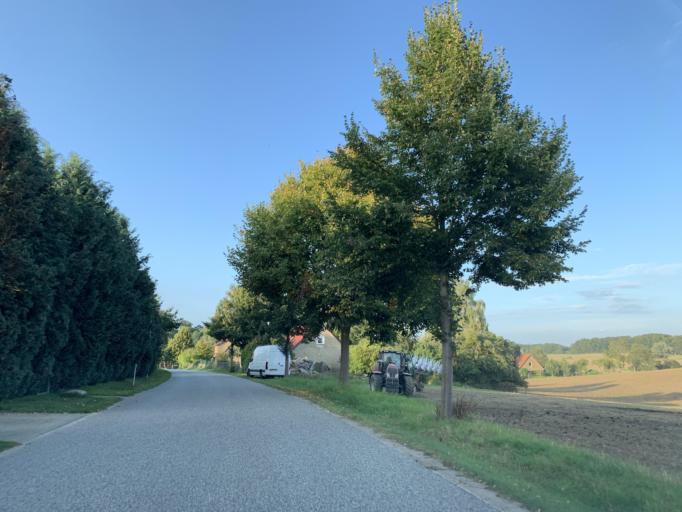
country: DE
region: Mecklenburg-Vorpommern
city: Loitz
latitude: 53.3641
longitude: 13.4432
